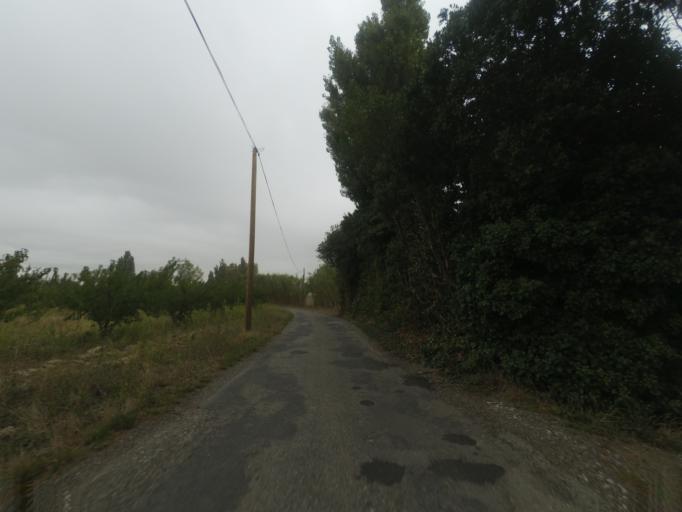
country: FR
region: Languedoc-Roussillon
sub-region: Departement des Pyrenees-Orientales
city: Saint-Esteve
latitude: 42.7010
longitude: 2.8407
